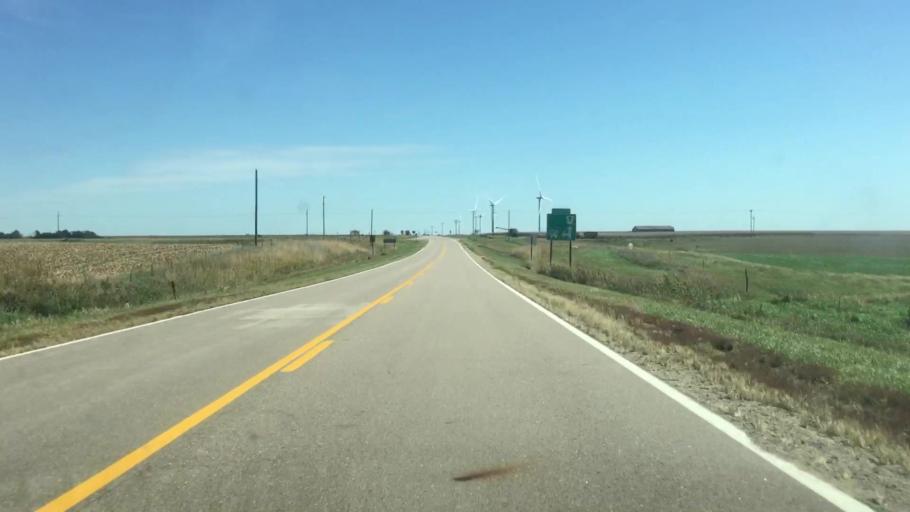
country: US
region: Kansas
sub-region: Washington County
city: Washington
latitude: 40.0449
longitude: -96.9385
